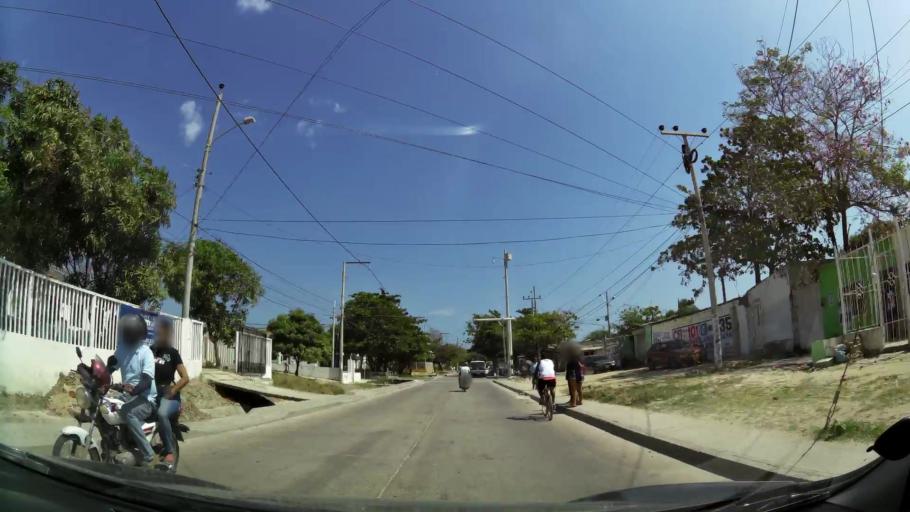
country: CO
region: Atlantico
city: Barranquilla
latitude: 10.9684
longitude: -74.8345
